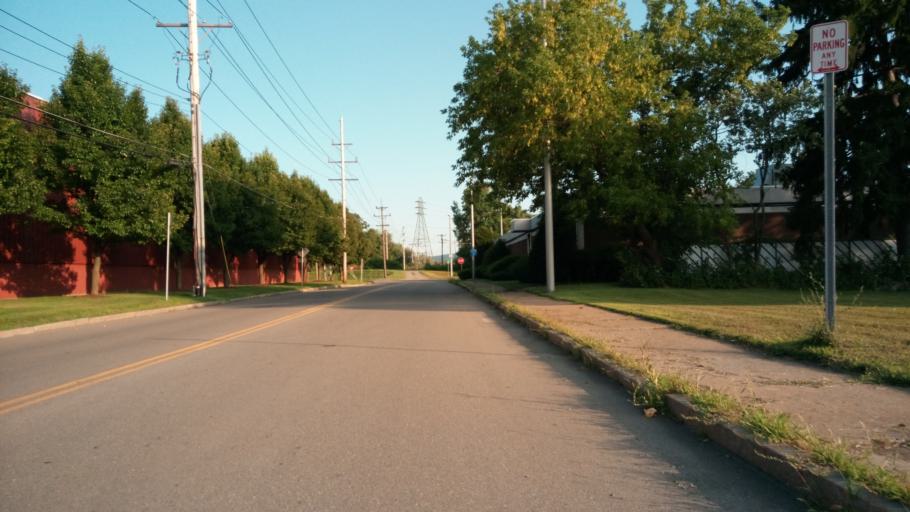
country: US
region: New York
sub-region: Chemung County
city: Elmira
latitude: 42.0907
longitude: -76.7894
